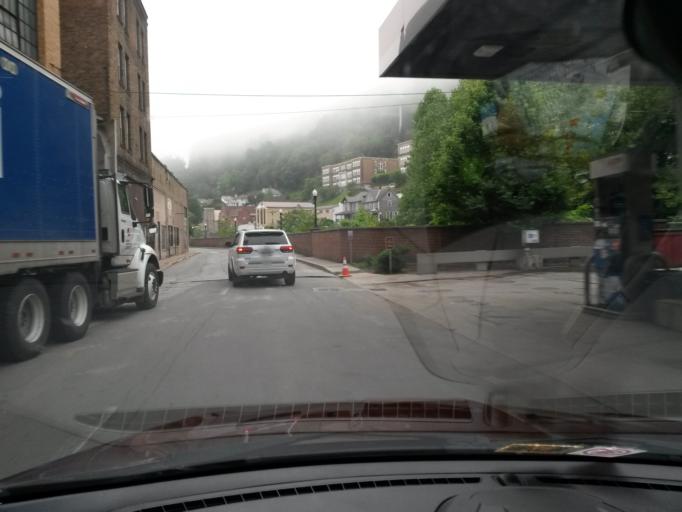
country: US
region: West Virginia
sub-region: McDowell County
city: Welch
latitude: 37.4310
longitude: -81.5853
